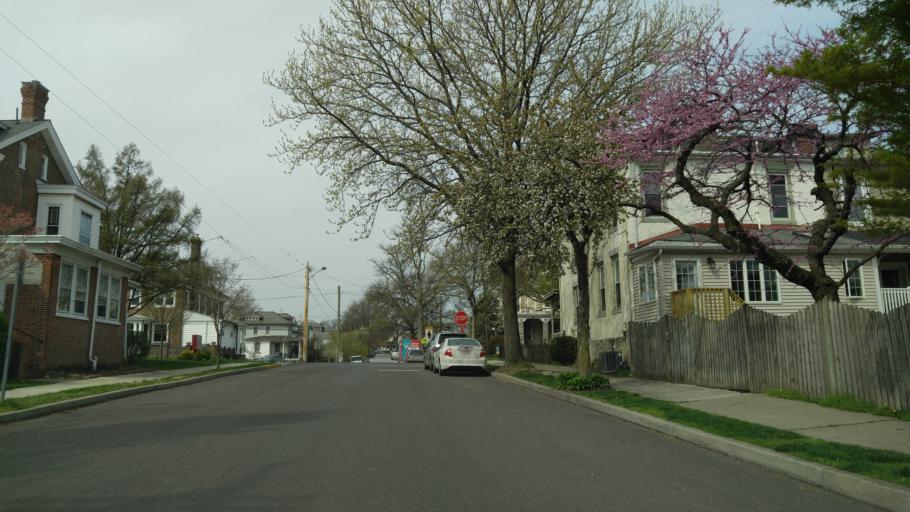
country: US
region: Pennsylvania
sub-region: Chester County
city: Phoenixville
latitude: 40.1273
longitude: -75.5161
